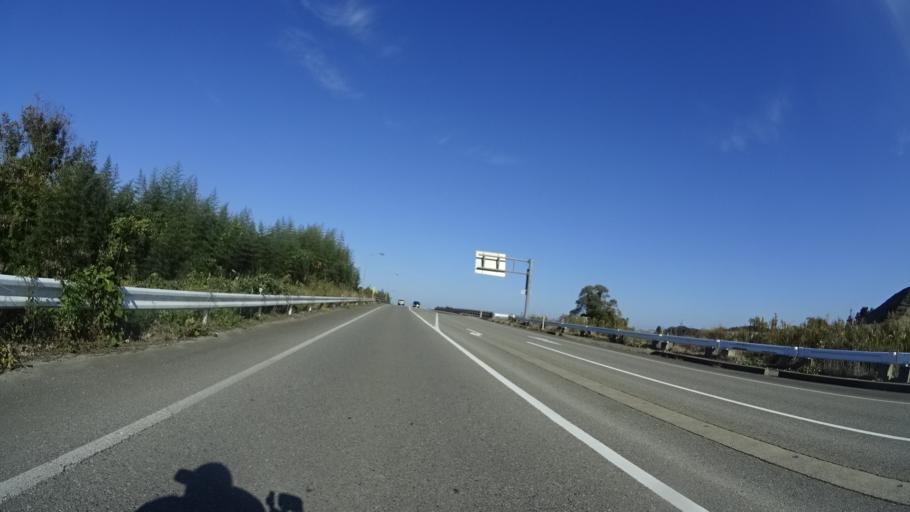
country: JP
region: Ishikawa
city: Komatsu
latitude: 36.3020
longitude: 136.3865
